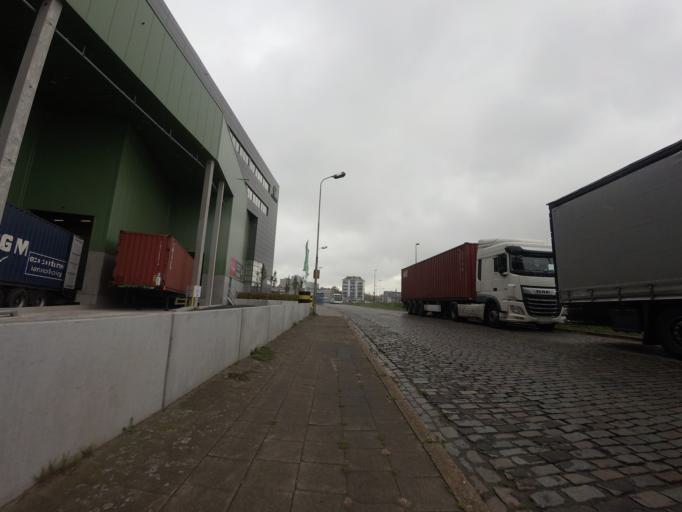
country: BE
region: Flanders
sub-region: Provincie Antwerpen
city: Borsbeek
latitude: 51.2343
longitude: 4.4569
